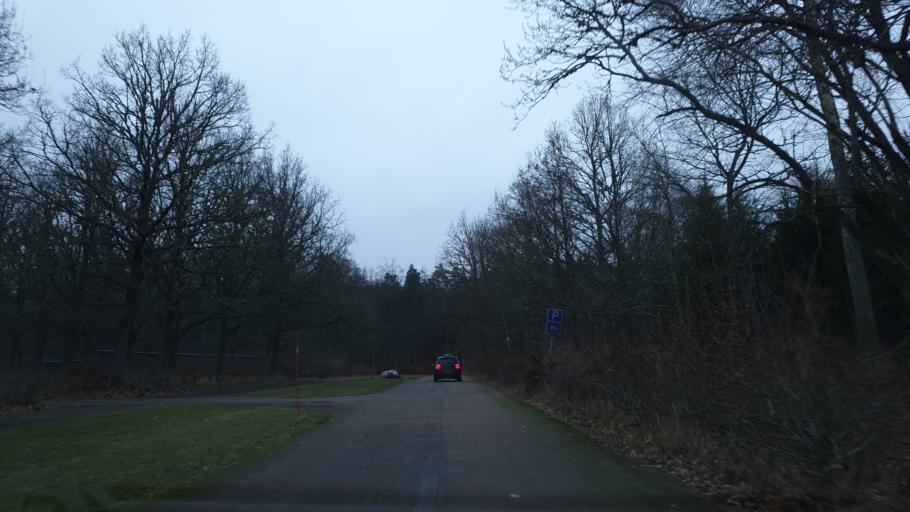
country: SE
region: Blekinge
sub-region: Karlskrona Kommun
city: Rodeby
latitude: 56.2133
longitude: 15.6833
